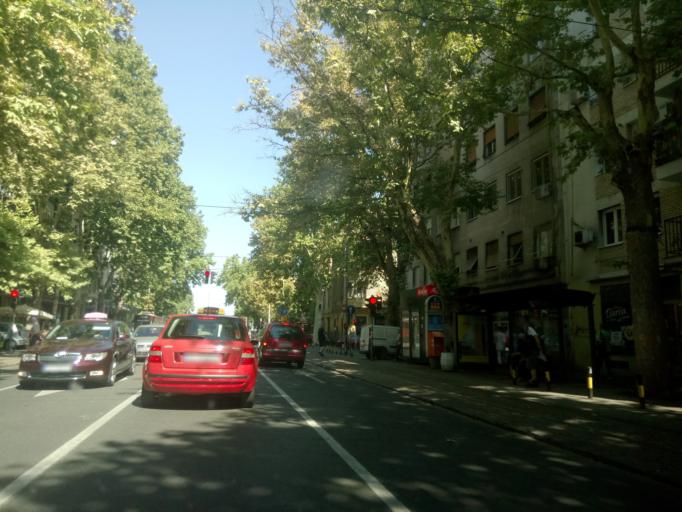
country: RS
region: Central Serbia
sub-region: Belgrade
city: Stari Grad
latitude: 44.8250
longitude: 20.4572
